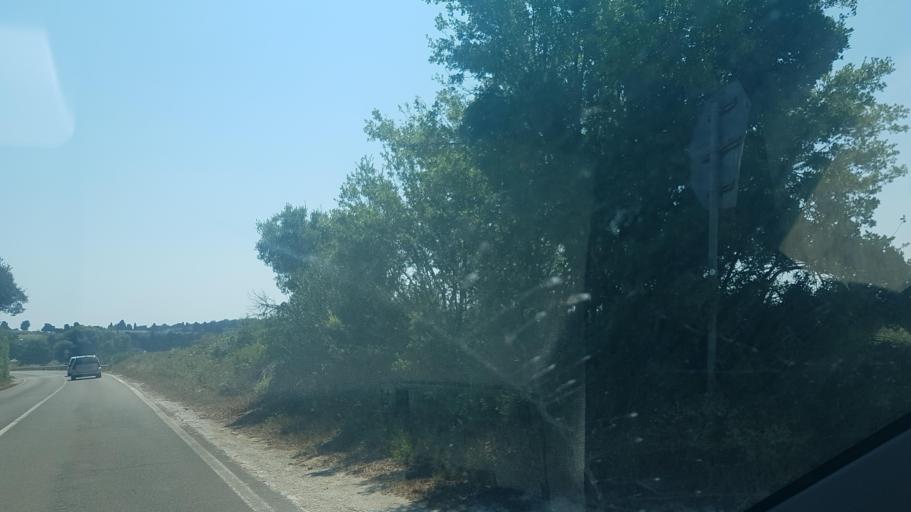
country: IT
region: Apulia
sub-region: Provincia di Lecce
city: Borgagne
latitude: 40.2247
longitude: 18.4341
